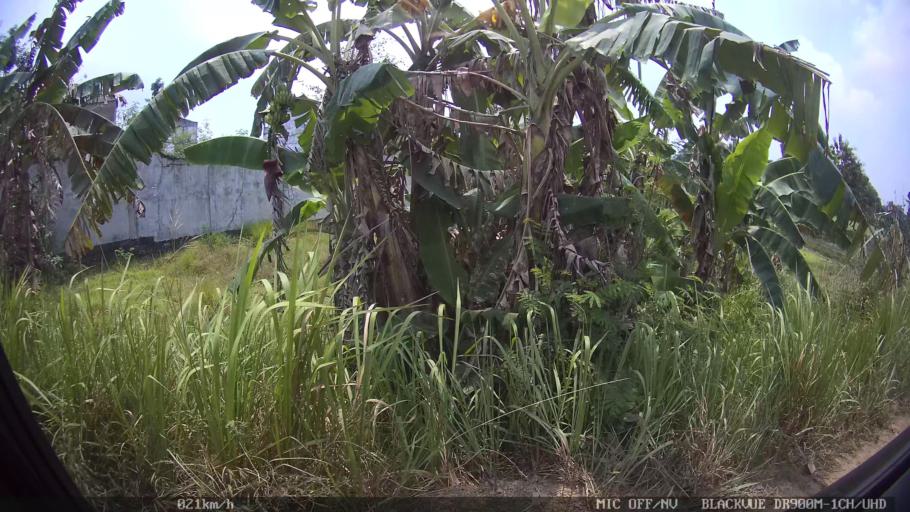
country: ID
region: Lampung
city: Pringsewu
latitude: -5.3705
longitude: 104.9976
